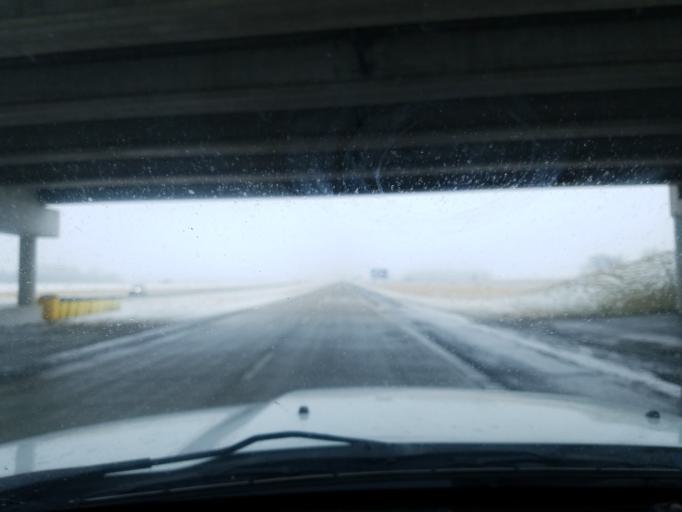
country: US
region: Indiana
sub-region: Howard County
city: Indian Heights
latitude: 40.4628
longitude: -86.0806
